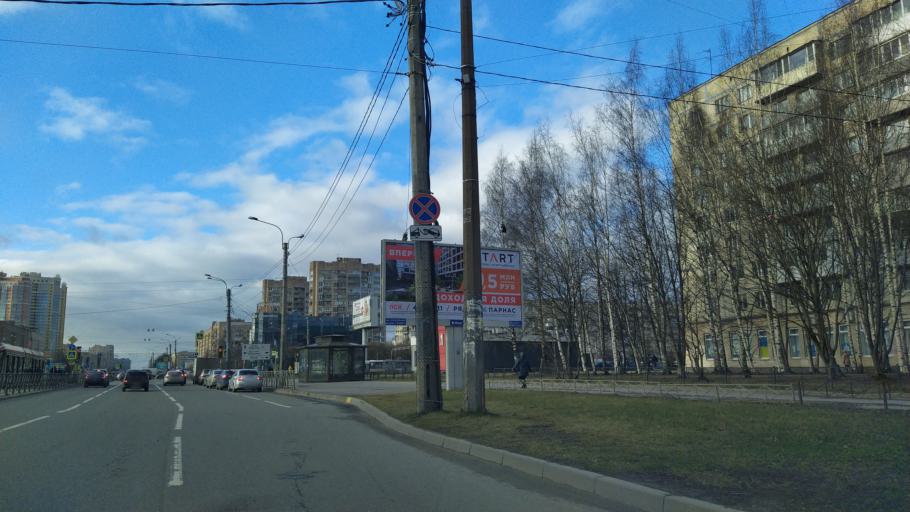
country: RU
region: St.-Petersburg
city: Grazhdanka
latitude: 60.0444
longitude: 30.3769
